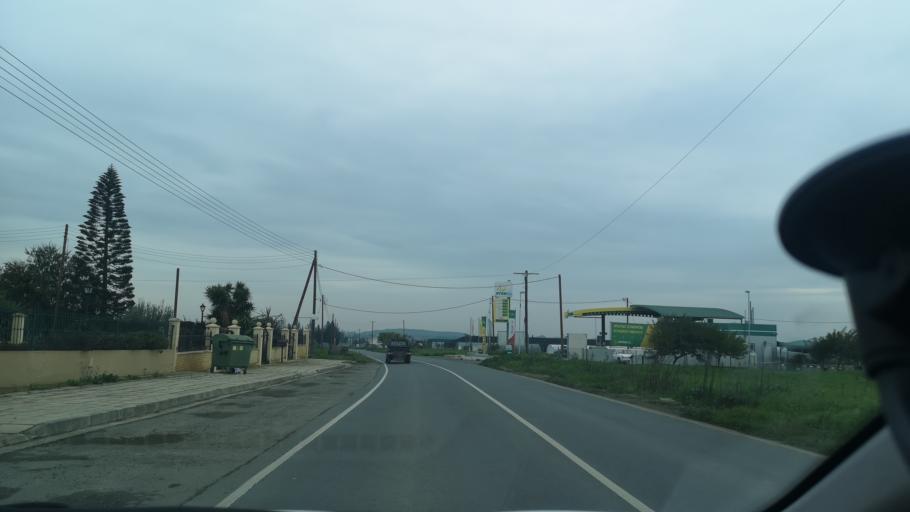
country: CY
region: Lefkosia
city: Tseri
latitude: 35.0798
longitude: 33.3057
